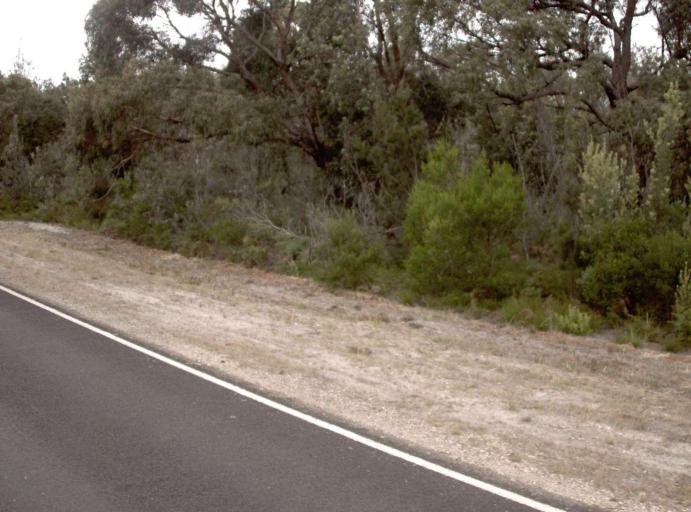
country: AU
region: Victoria
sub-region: East Gippsland
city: Bairnsdale
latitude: -38.0641
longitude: 147.5586
